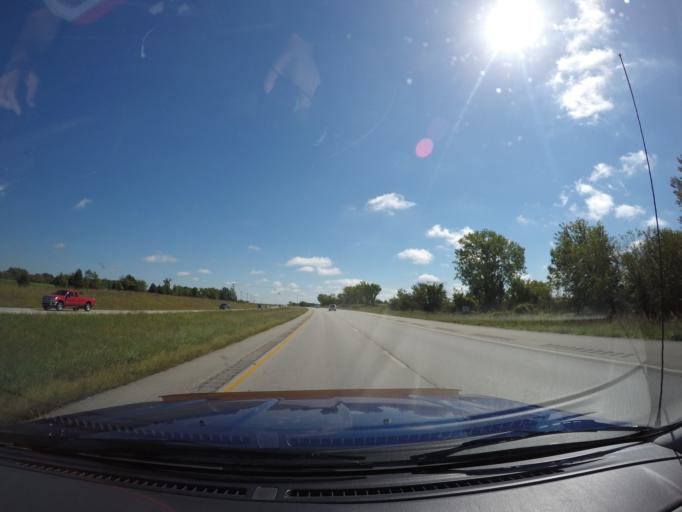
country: US
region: Kansas
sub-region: Douglas County
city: Eudora
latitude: 38.9290
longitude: -95.1047
